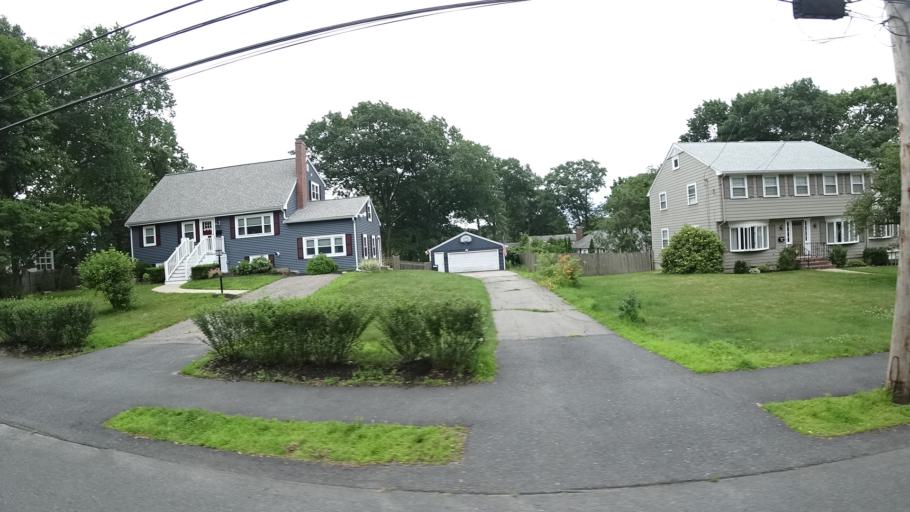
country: US
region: Massachusetts
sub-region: Norfolk County
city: Dedham
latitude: 42.2283
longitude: -71.1514
